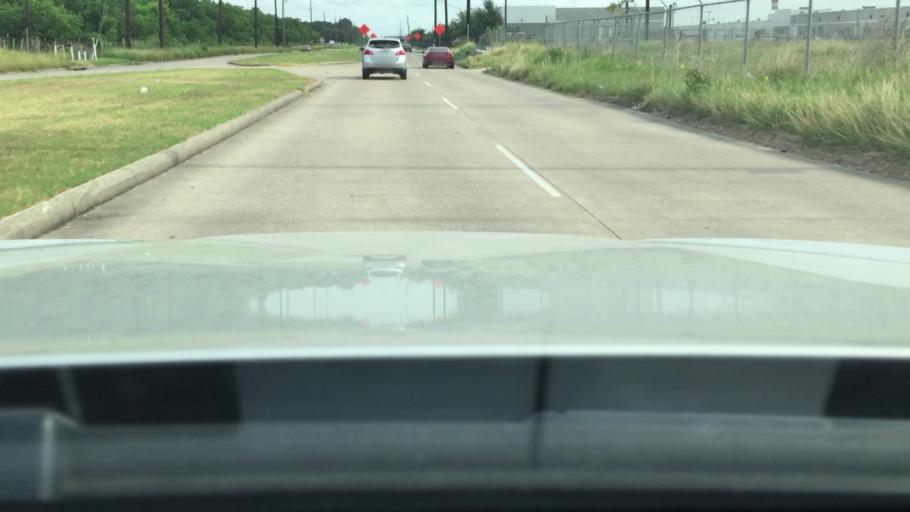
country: US
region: Texas
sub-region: Harris County
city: Jersey Village
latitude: 29.9378
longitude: -95.5467
